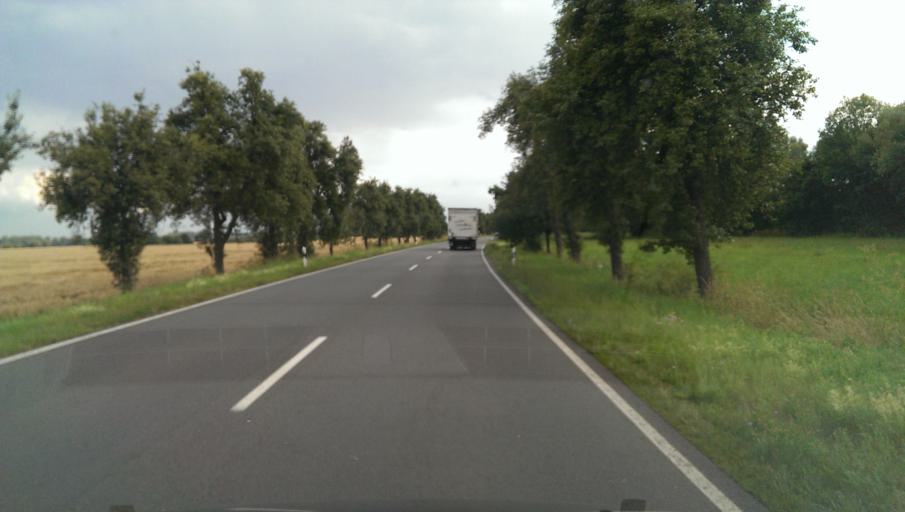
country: DE
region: Saxony
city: Elstertrebnitz
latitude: 51.1503
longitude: 12.2467
